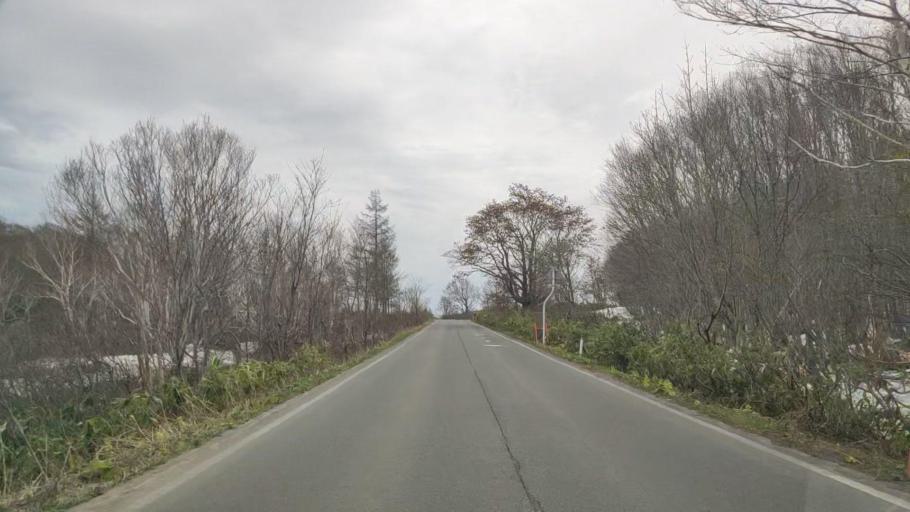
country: JP
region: Aomori
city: Aomori Shi
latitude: 40.6888
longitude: 140.9228
